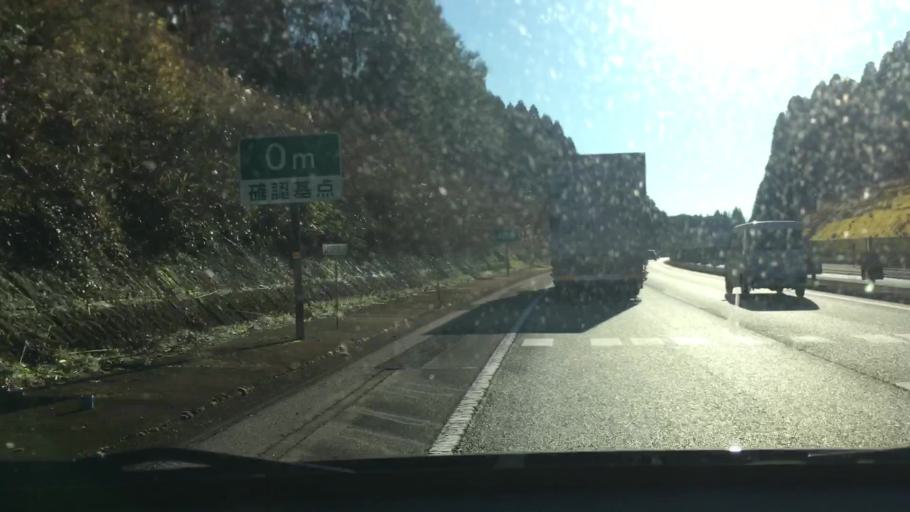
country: JP
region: Kagoshima
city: Kajiki
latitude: 31.8717
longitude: 130.6929
